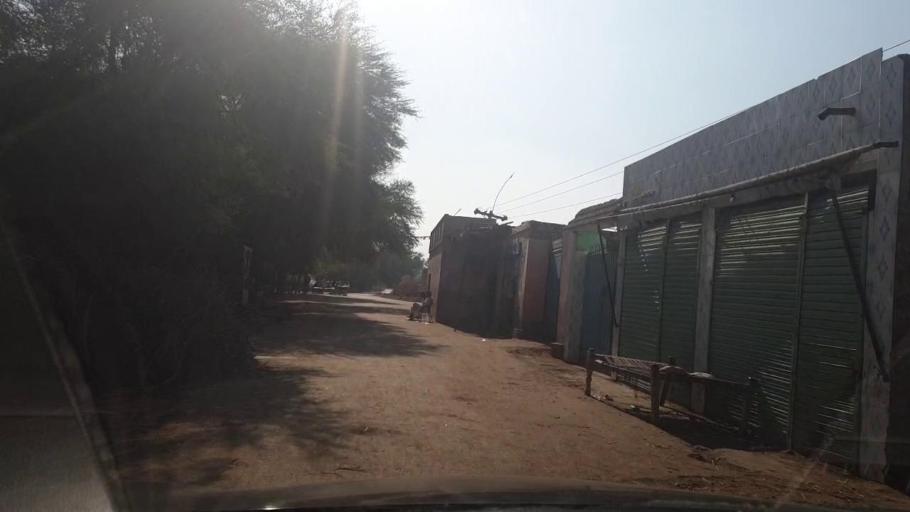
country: PK
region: Sindh
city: Ubauro
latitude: 28.1351
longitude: 69.6483
